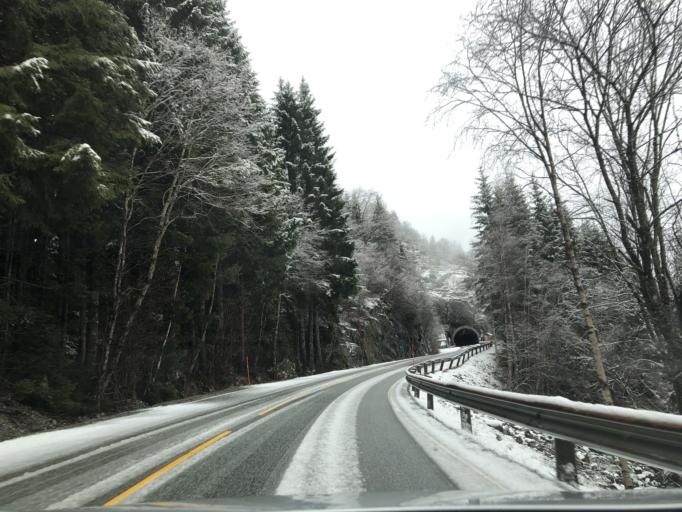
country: NO
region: Rogaland
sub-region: Sauda
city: Sauda
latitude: 59.5284
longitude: 6.5925
